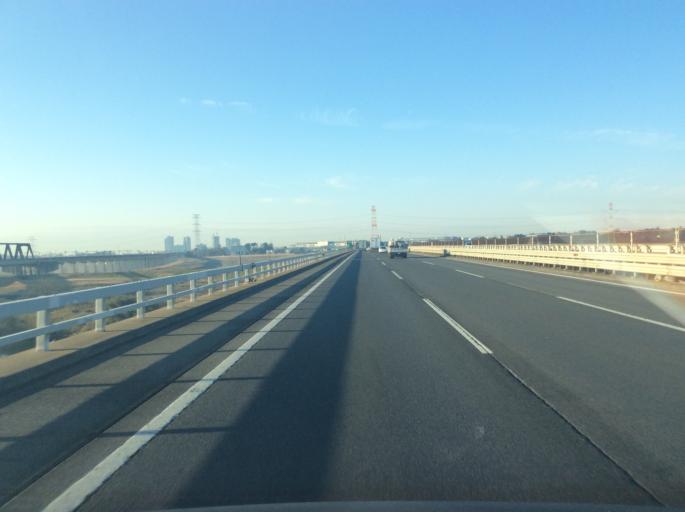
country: JP
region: Ibaraki
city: Moriya
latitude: 35.9296
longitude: 139.9624
